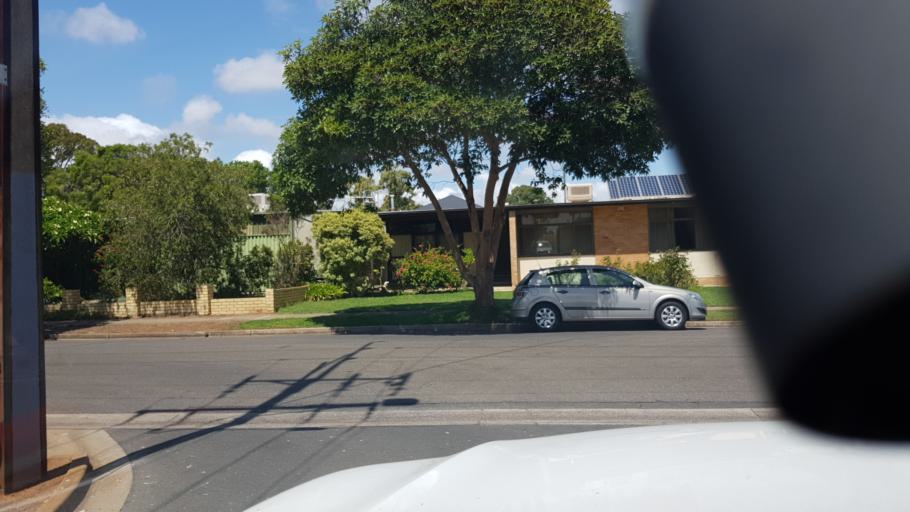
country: AU
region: South Australia
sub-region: Holdfast Bay
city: North Brighton
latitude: -35.0057
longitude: 138.5288
